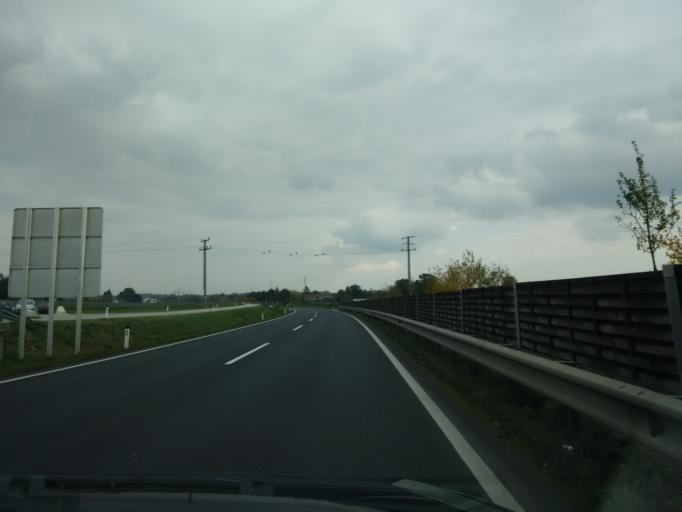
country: AT
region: Upper Austria
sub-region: Politischer Bezirk Vocklabruck
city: Oberndorf bei Schwanenstadt
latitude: 48.0475
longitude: 13.7654
